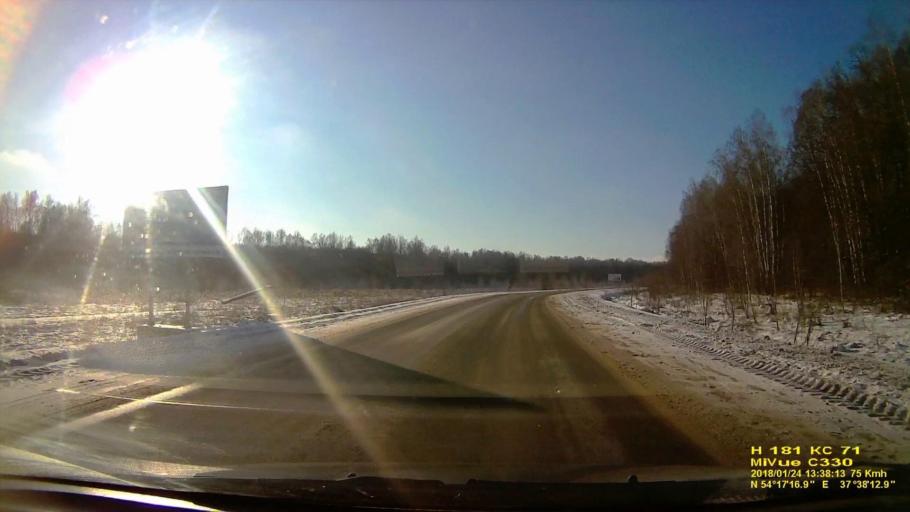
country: RU
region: Tula
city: Gorelki
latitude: 54.2880
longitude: 37.6368
